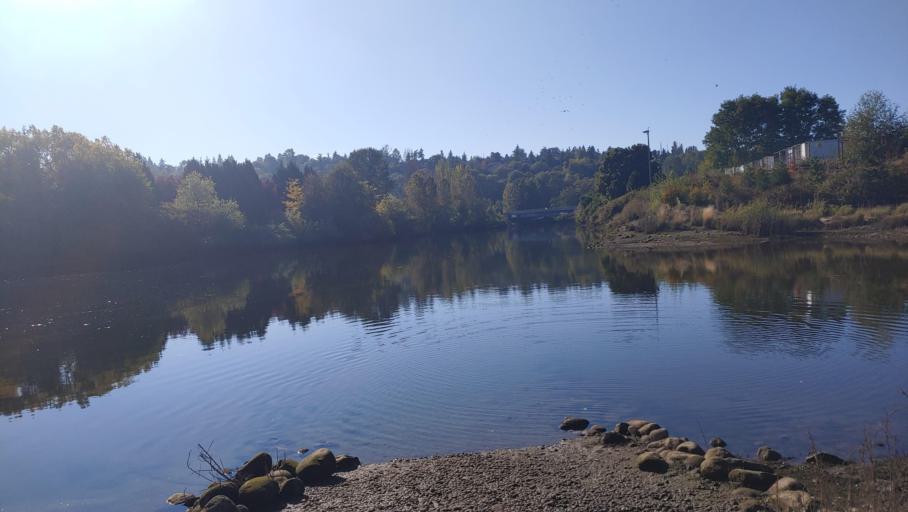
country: US
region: Washington
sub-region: King County
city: Riverton
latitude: 47.5010
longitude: -122.2895
